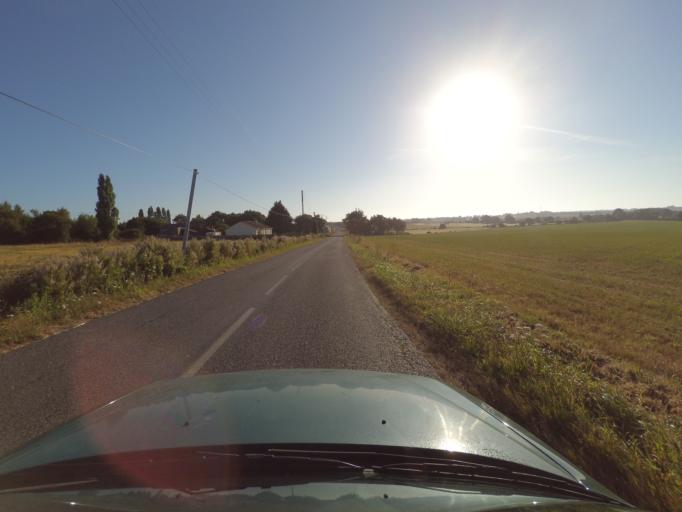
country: FR
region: Pays de la Loire
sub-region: Departement de la Loire-Atlantique
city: Le Bignon
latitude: 47.0859
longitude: -1.4615
